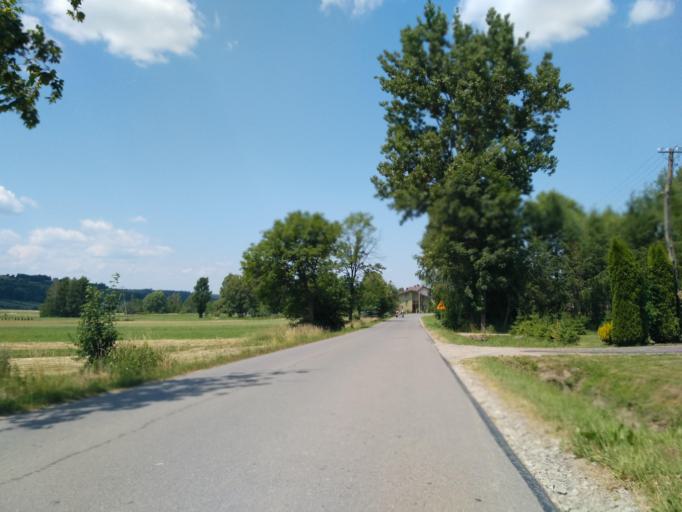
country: PL
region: Subcarpathian Voivodeship
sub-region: Powiat sanocki
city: Niebieszczany
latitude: 49.4955
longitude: 22.1678
